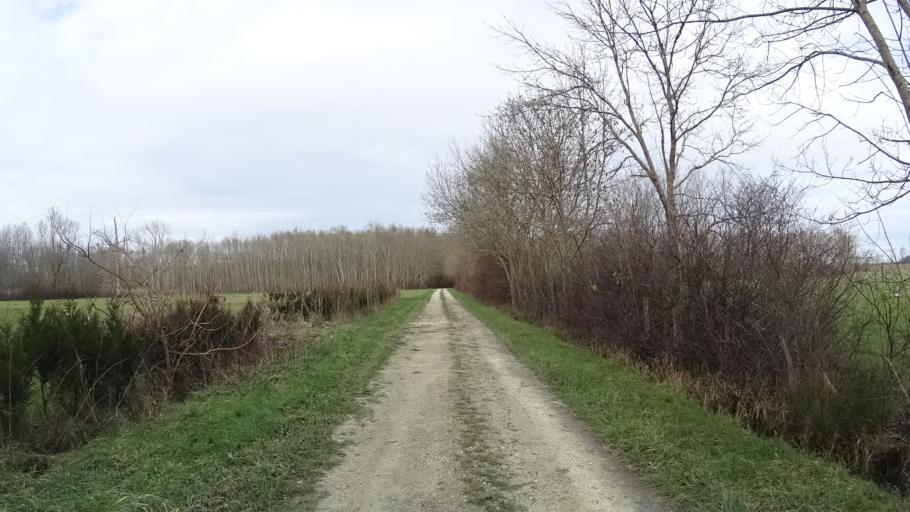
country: FR
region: Aquitaine
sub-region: Departement de la Dordogne
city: Saint-Aulaye
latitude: 45.2135
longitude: 0.1383
